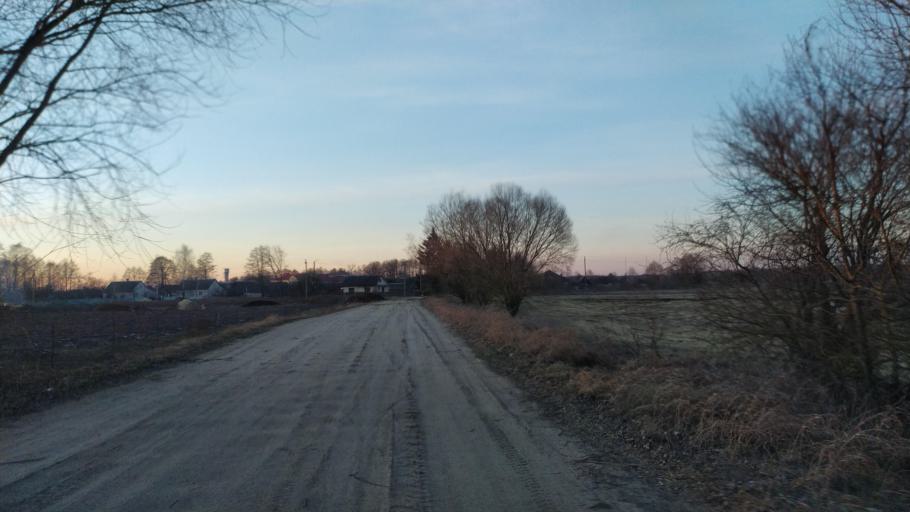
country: BY
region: Brest
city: Pruzhany
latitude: 52.5512
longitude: 24.2312
